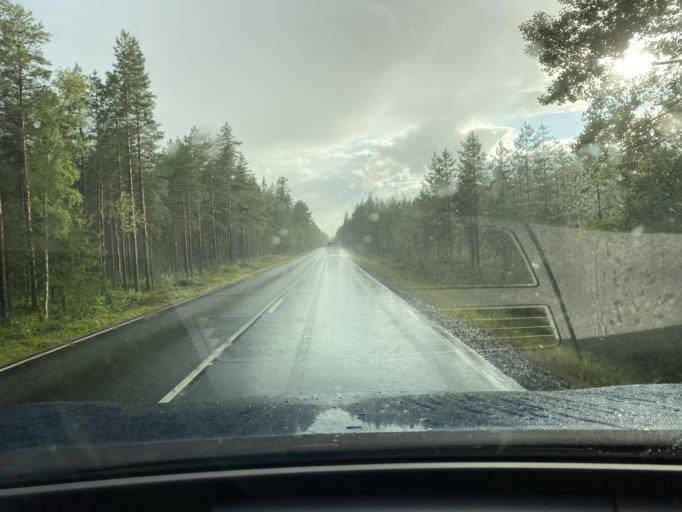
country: FI
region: Southern Ostrobothnia
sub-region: Seinaejoki
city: Kurikka
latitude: 62.4831
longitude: 22.4977
